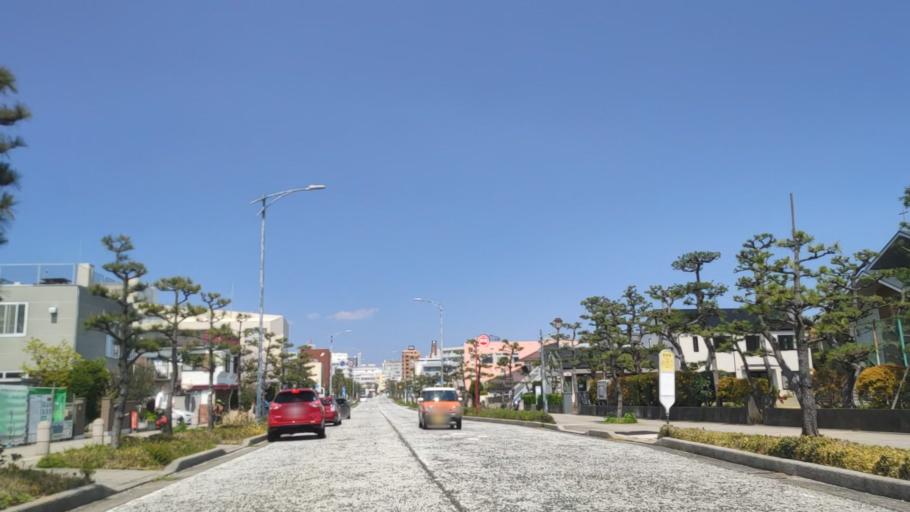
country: JP
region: Kanagawa
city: Hiratsuka
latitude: 35.3214
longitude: 139.3529
